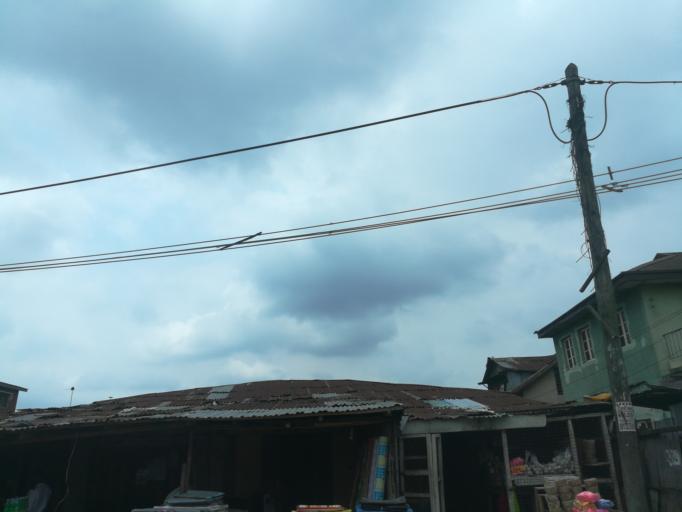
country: NG
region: Lagos
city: Agege
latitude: 6.6191
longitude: 3.3260
